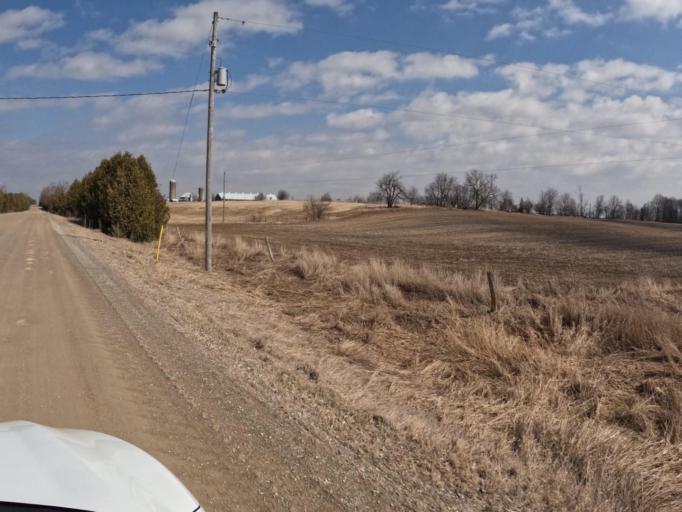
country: CA
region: Ontario
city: Orangeville
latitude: 43.9202
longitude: -80.2554
